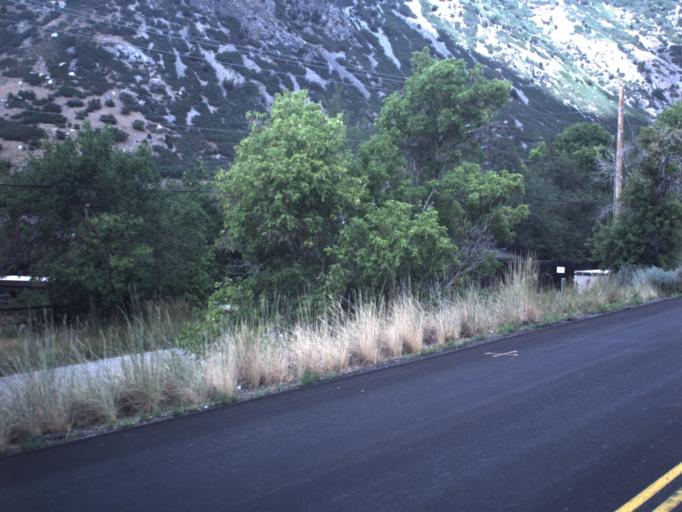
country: US
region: Utah
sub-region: Salt Lake County
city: Granite
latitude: 40.5729
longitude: -111.7901
